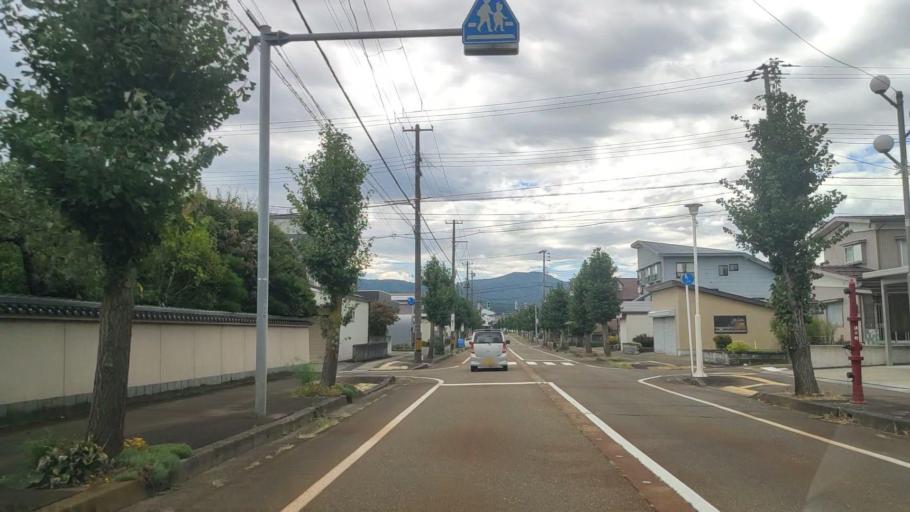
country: JP
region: Niigata
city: Arai
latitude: 37.0238
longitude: 138.2463
